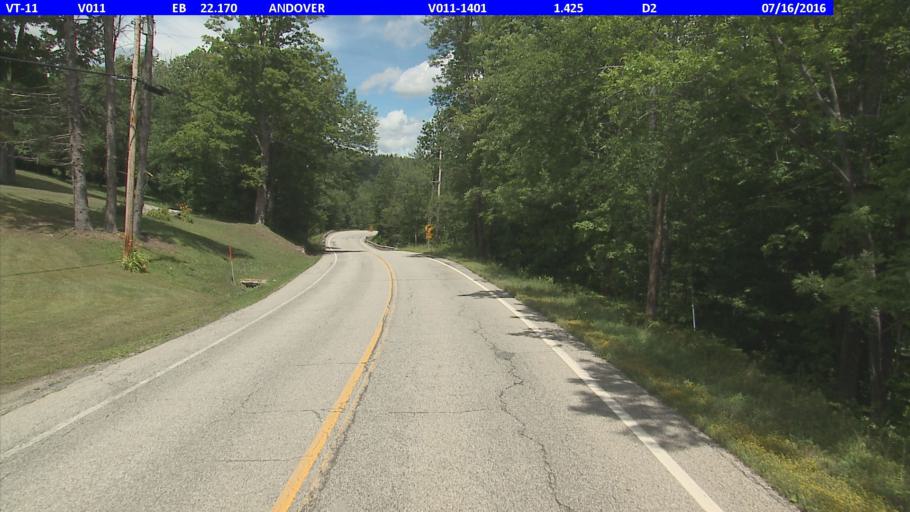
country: US
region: Vermont
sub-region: Windsor County
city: Chester
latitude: 43.2523
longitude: -72.7194
